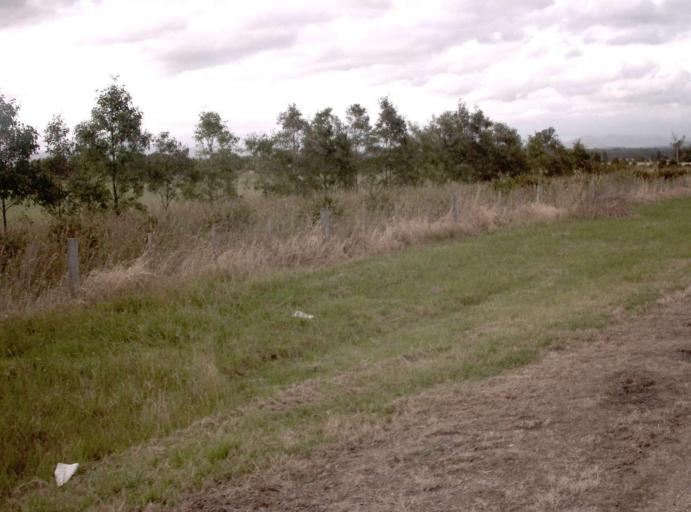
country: AU
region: Victoria
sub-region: Wellington
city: Sale
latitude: -37.8437
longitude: 147.0555
